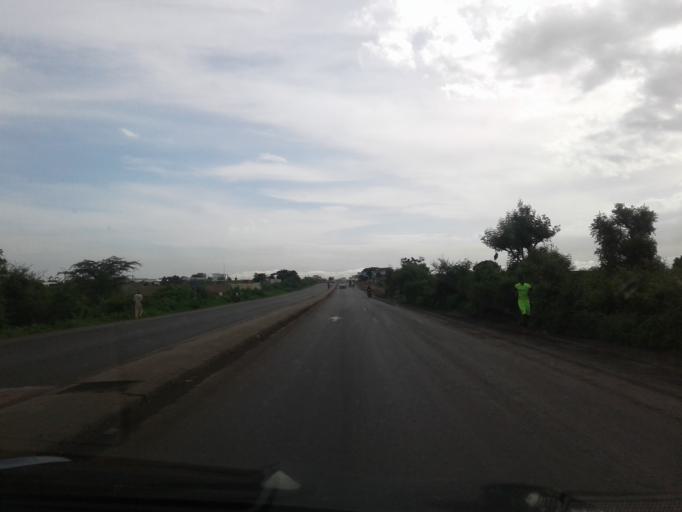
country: SN
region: Thies
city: Pout
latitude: 14.7132
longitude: -17.1949
